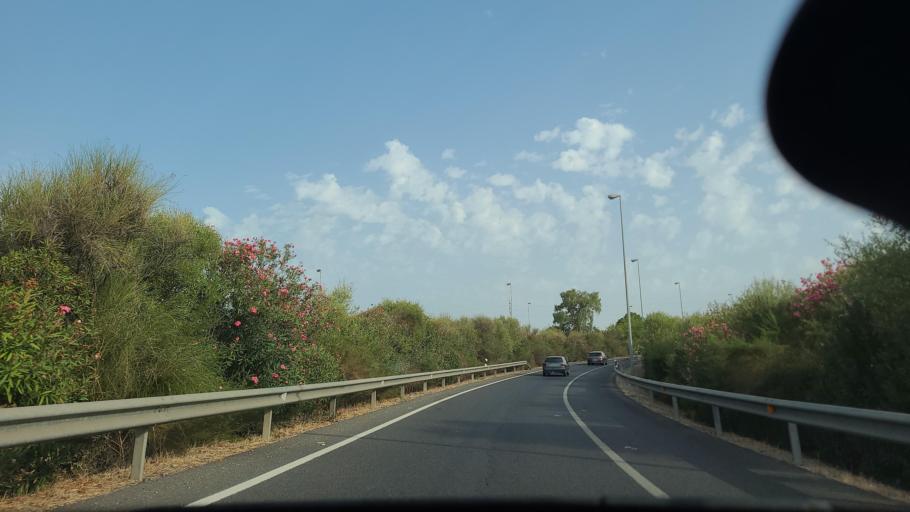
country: ES
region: Andalusia
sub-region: Province of Cordoba
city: Cordoba
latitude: 37.9068
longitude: -4.7533
